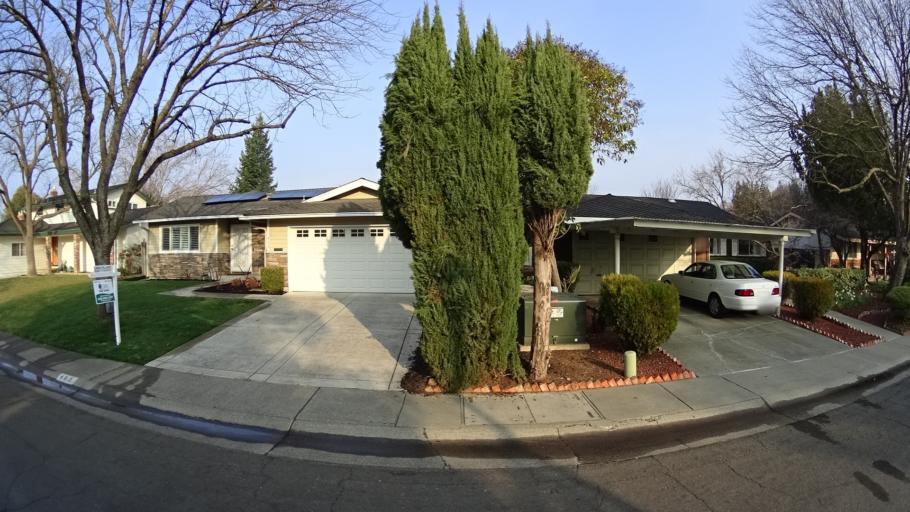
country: US
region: California
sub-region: Yolo County
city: Davis
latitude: 38.5639
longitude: -121.7500
